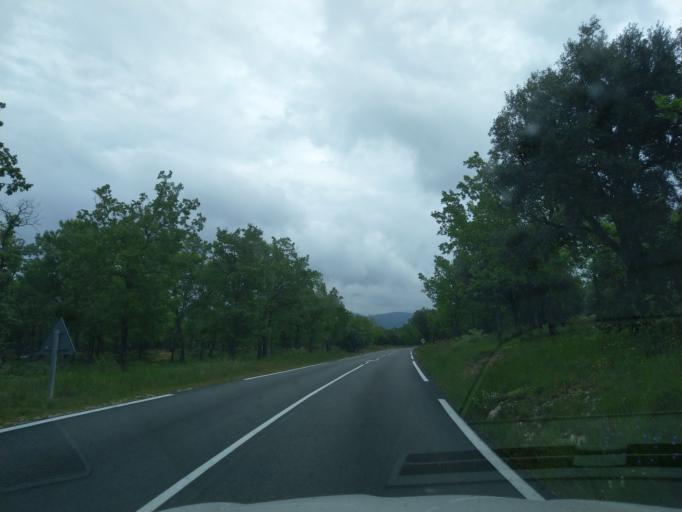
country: FR
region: Provence-Alpes-Cote d'Azur
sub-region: Departement du Var
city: Signes
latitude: 43.2763
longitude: 5.8056
